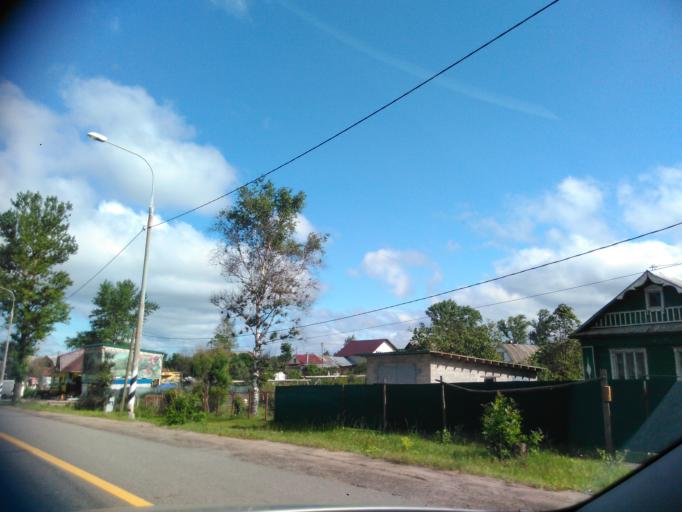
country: RU
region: Moskovskaya
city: Klin
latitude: 56.2832
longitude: 36.8231
